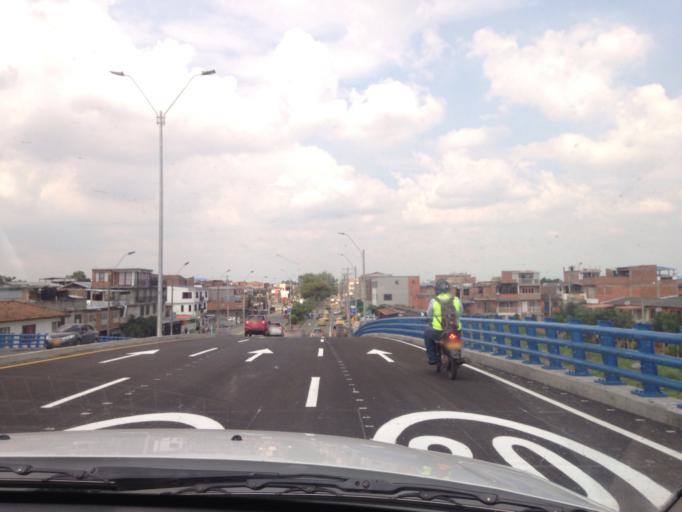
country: CO
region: Valle del Cauca
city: Cali
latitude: 3.3941
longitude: -76.5128
